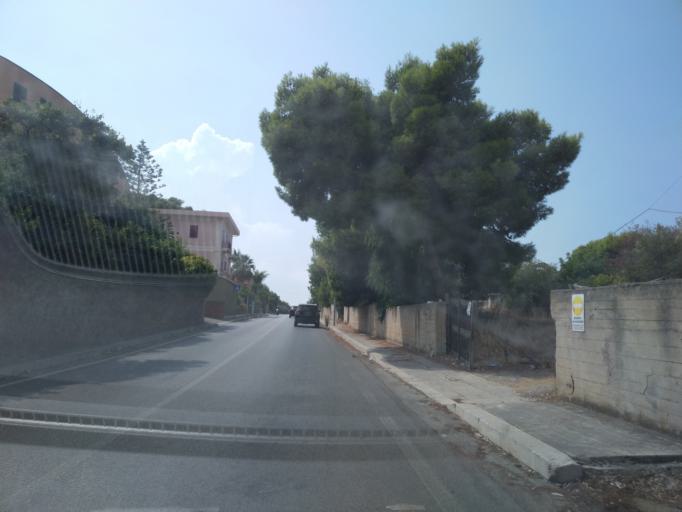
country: IT
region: Sicily
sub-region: Palermo
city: Cefalu
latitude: 38.0312
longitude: 14.0063
